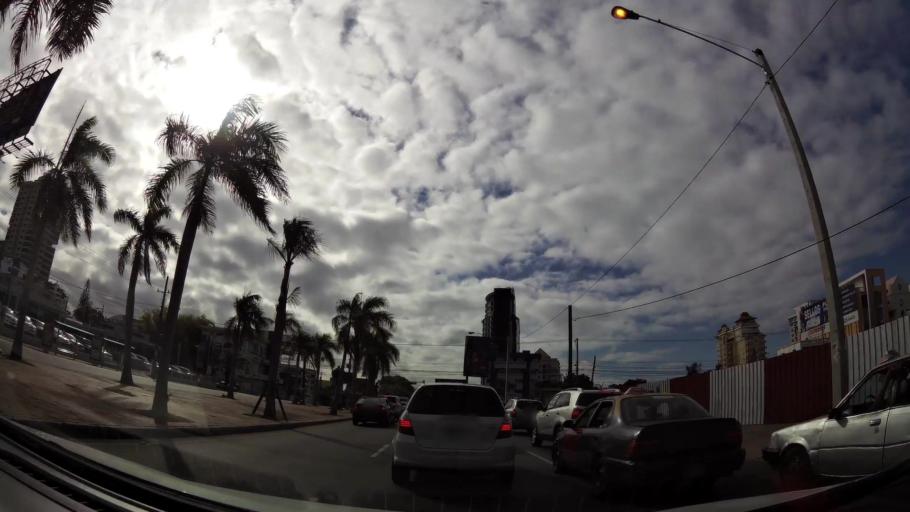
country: DO
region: Nacional
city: La Julia
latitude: 18.4607
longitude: -69.9344
